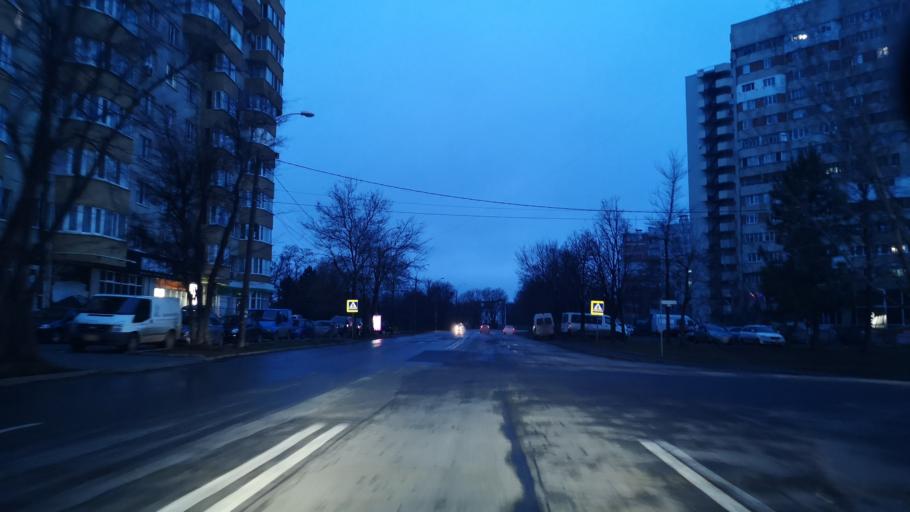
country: MD
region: Chisinau
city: Chisinau
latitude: 47.0321
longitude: 28.8787
